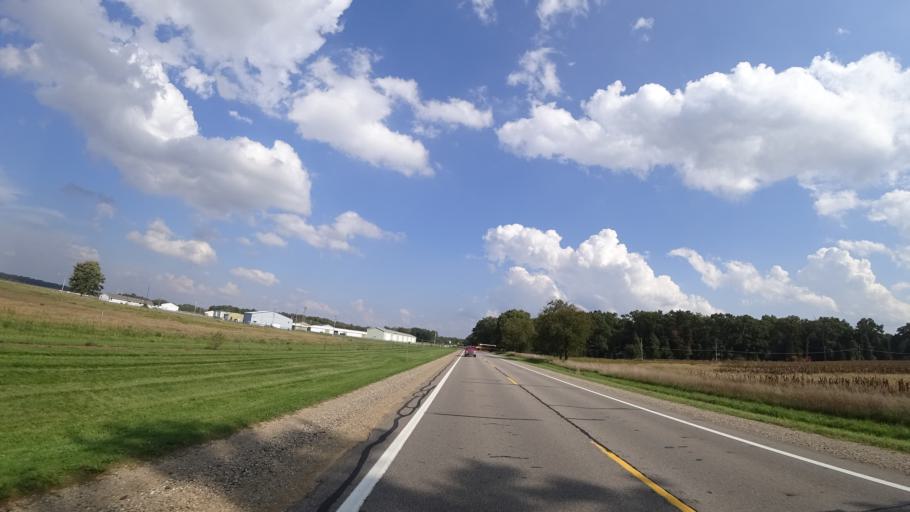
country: US
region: Michigan
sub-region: Saint Joseph County
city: Three Rivers
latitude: 41.9549
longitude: -85.5932
